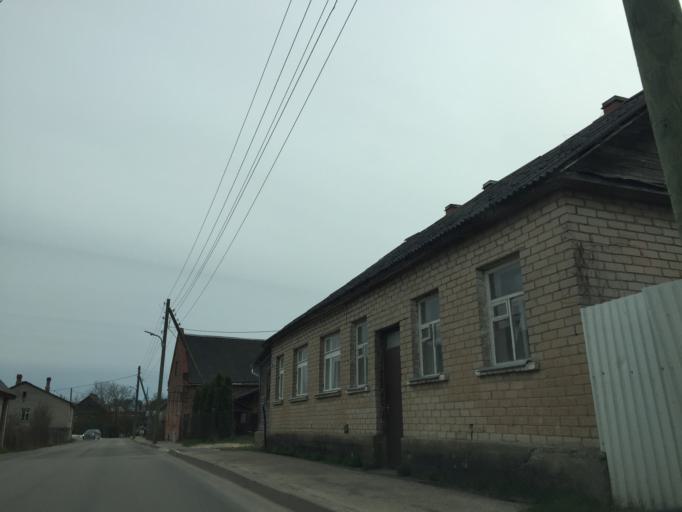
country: LV
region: Ludzas Rajons
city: Ludza
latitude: 56.5518
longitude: 27.7279
